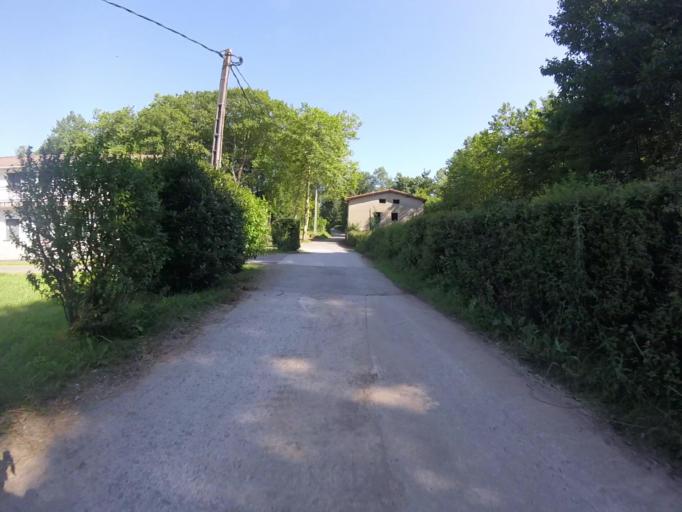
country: ES
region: Basque Country
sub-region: Provincia de Guipuzcoa
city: Astigarraga
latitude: 43.2691
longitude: -1.9318
